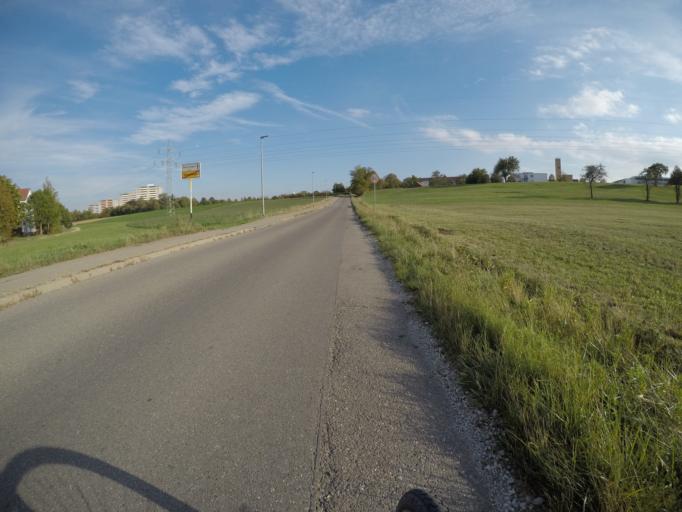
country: DE
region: Baden-Wuerttemberg
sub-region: Tuebingen Region
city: Sickenhausen
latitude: 48.5244
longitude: 9.1983
